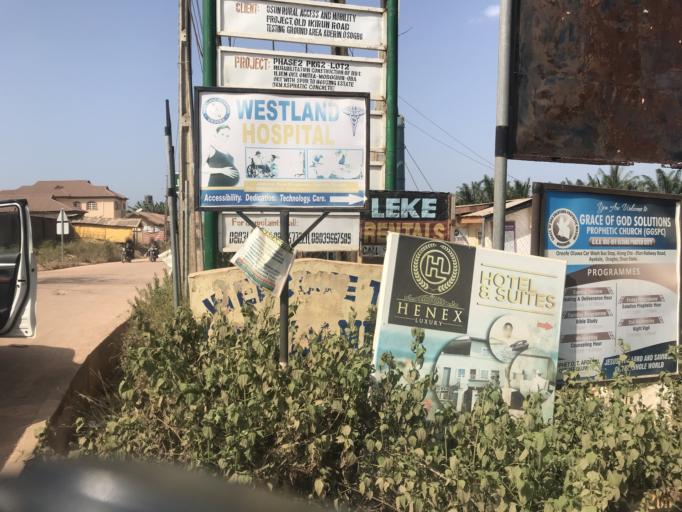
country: NG
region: Osun
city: Osogbo
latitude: 7.7921
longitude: 4.5782
